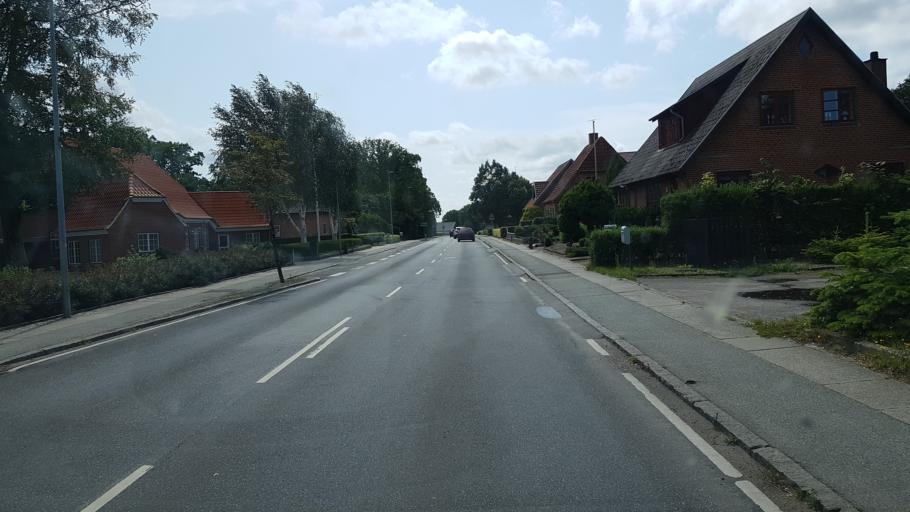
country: DK
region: South Denmark
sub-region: Vejen Kommune
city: Vejen
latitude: 55.5690
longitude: 9.1367
